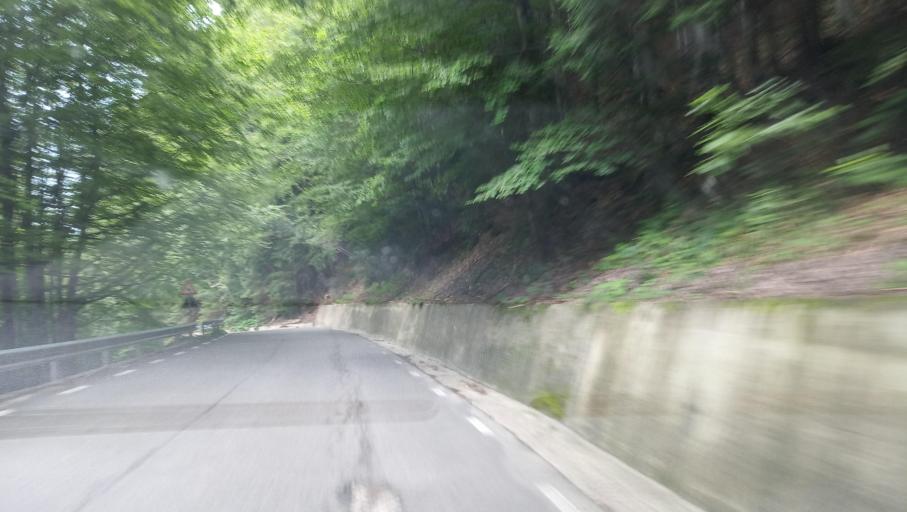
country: RO
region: Prahova
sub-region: Oras Sinaia
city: Sinaia
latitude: 45.3204
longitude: 25.4942
